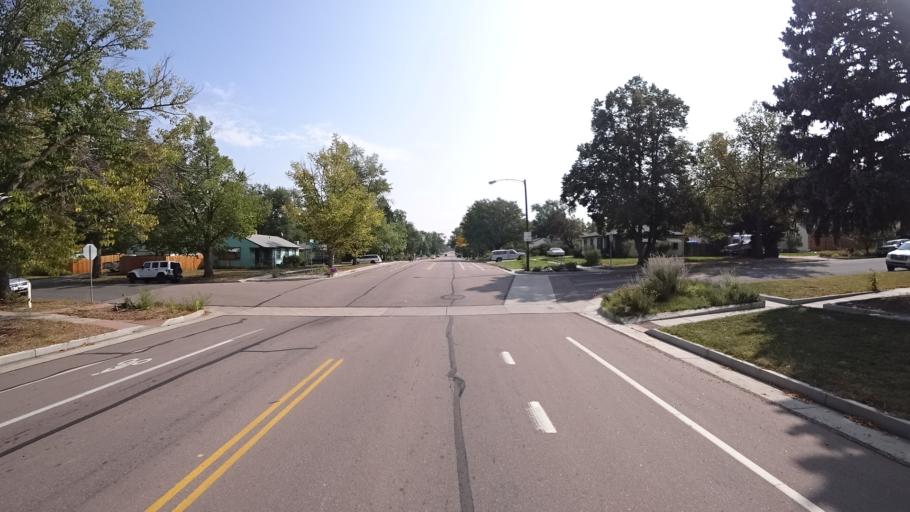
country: US
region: Colorado
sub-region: El Paso County
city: Colorado Springs
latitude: 38.8360
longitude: -104.8009
